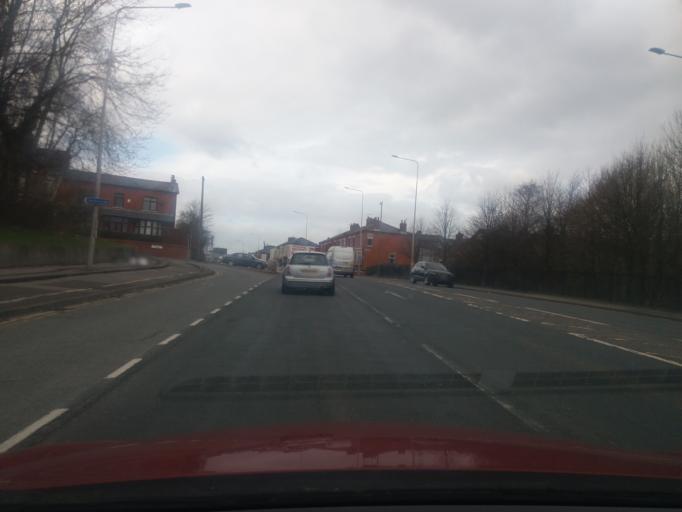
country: GB
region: England
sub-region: Lancashire
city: Preston
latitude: 53.7556
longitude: -2.6818
